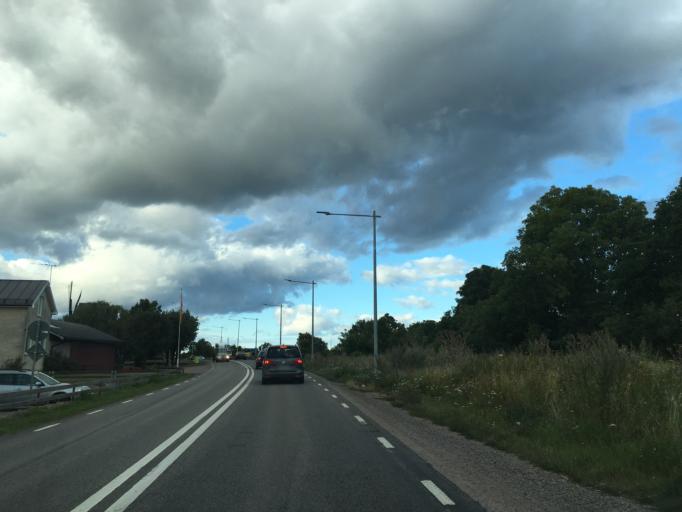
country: SE
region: Kalmar
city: Faerjestaden
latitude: 56.6503
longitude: 16.5179
